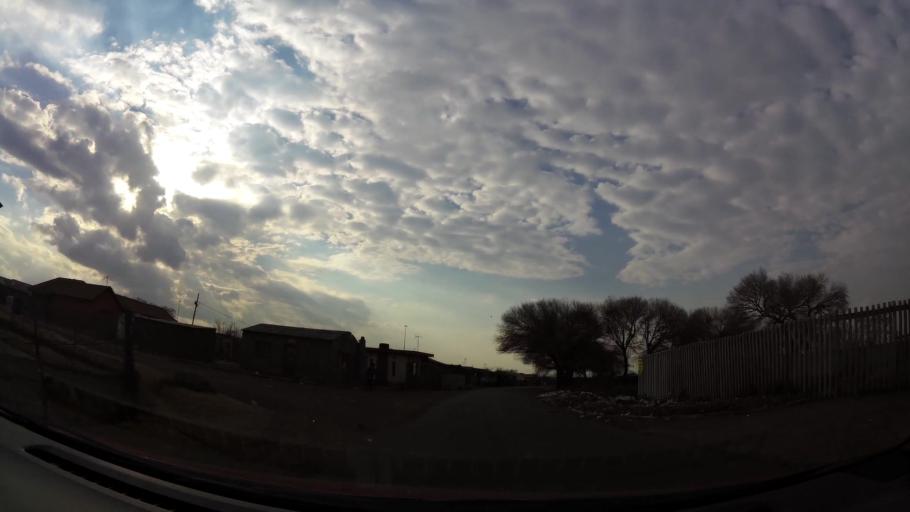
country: ZA
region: Gauteng
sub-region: Sedibeng District Municipality
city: Vanderbijlpark
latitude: -26.6917
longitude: 27.8770
